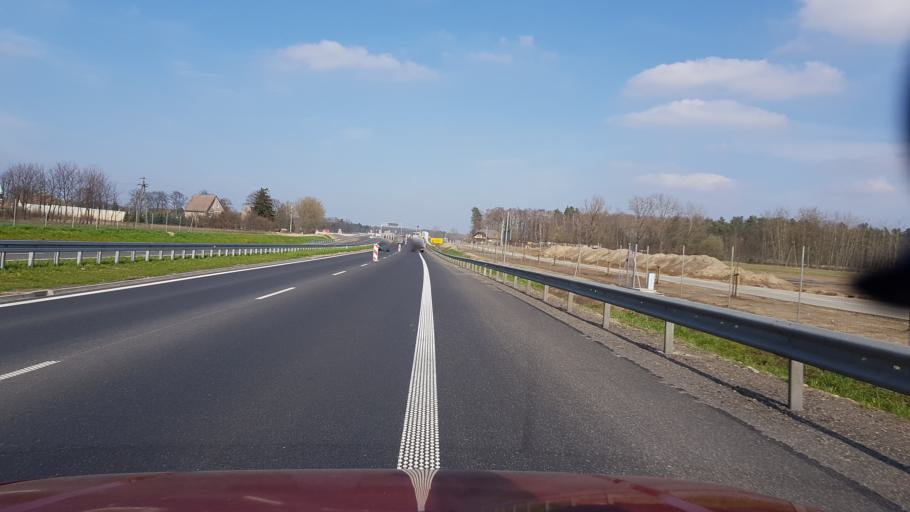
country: PL
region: West Pomeranian Voivodeship
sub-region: Powiat goleniowski
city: Nowogard
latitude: 53.6467
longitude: 15.0697
